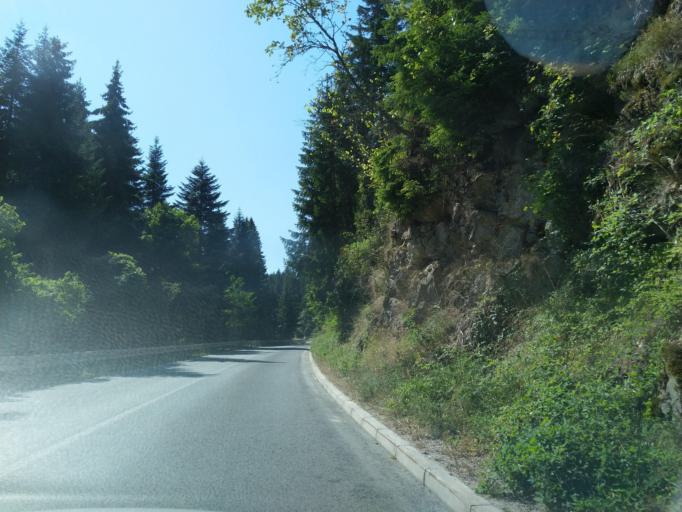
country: RS
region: Central Serbia
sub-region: Zlatiborski Okrug
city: Nova Varos
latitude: 43.4171
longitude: 19.8297
